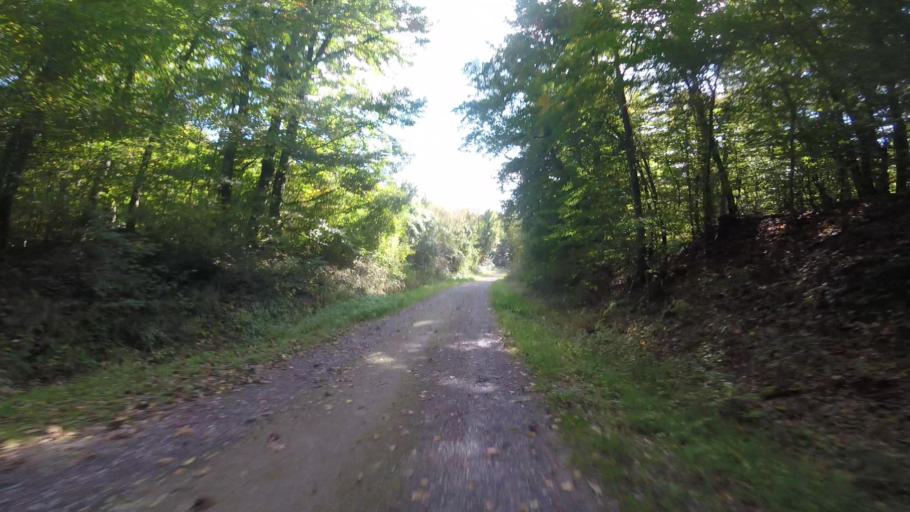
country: DE
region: Baden-Wuerttemberg
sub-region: Regierungsbezirk Stuttgart
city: Kirchberg an der Murr
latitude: 48.9851
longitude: 9.3359
